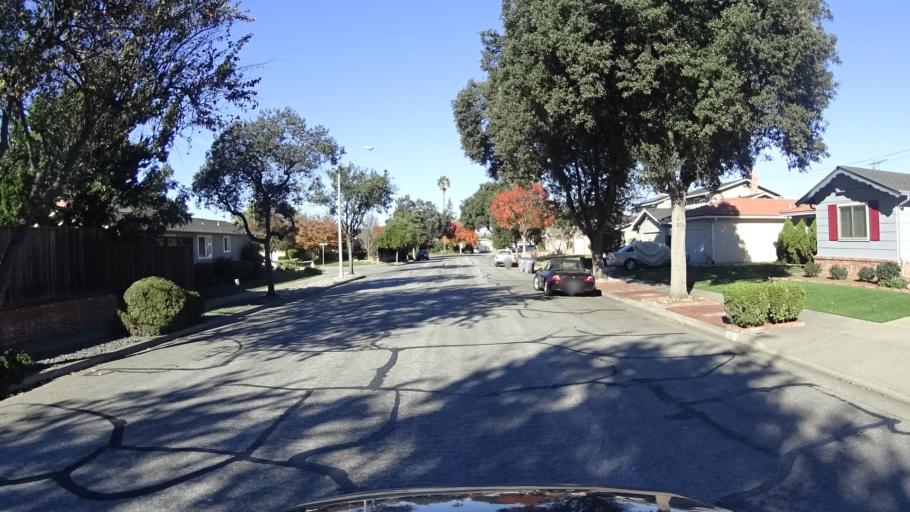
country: US
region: California
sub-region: Santa Clara County
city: Sunnyvale
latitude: 37.3476
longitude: -122.0238
